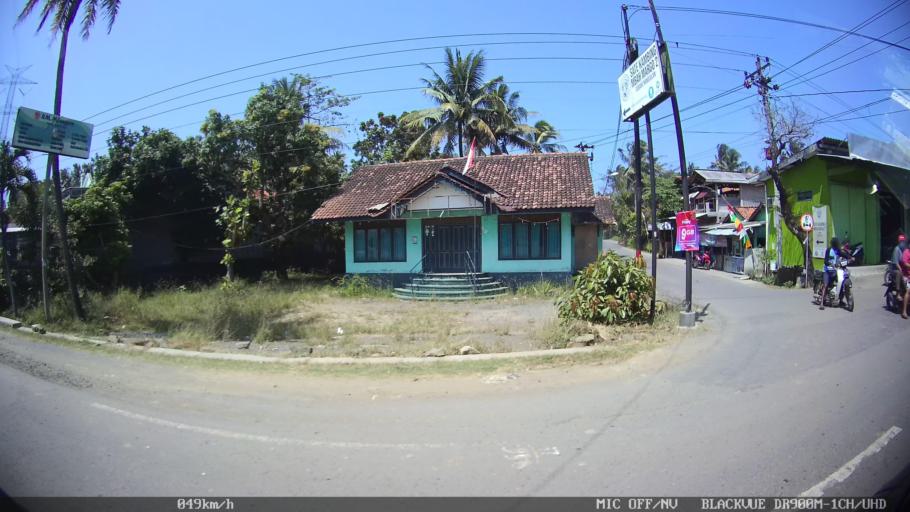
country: ID
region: Daerah Istimewa Yogyakarta
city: Srandakan
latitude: -7.8867
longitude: 110.0576
